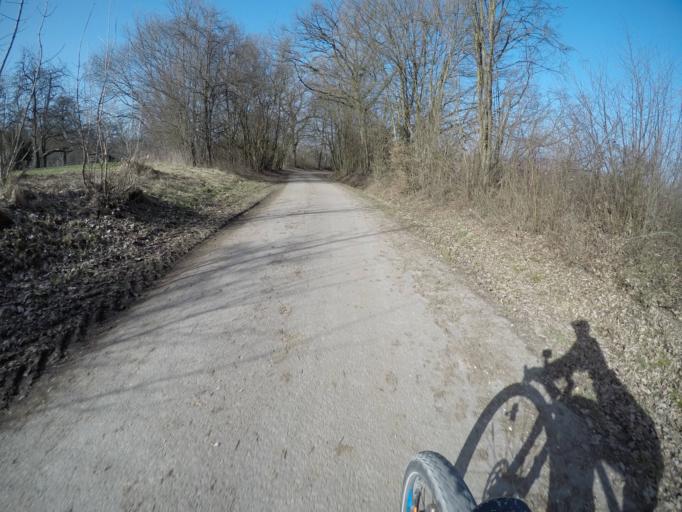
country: DE
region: Baden-Wuerttemberg
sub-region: Regierungsbezirk Stuttgart
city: Hochdorf
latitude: 48.6849
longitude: 9.4651
